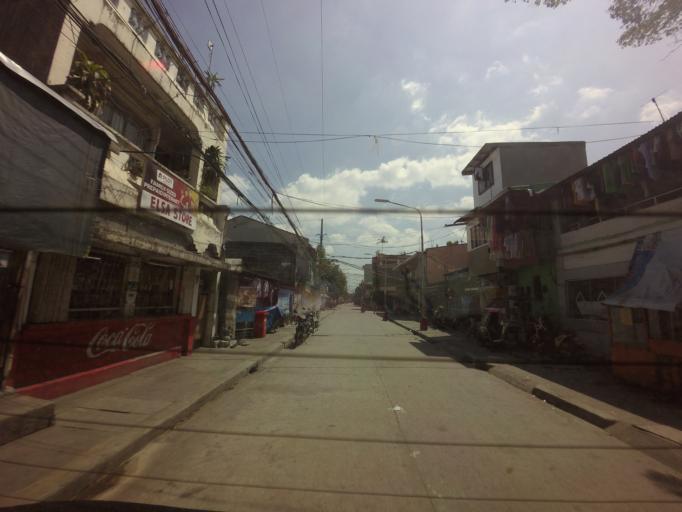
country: PH
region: Metro Manila
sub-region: Caloocan City
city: Niugan
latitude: 14.6486
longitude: 120.9578
